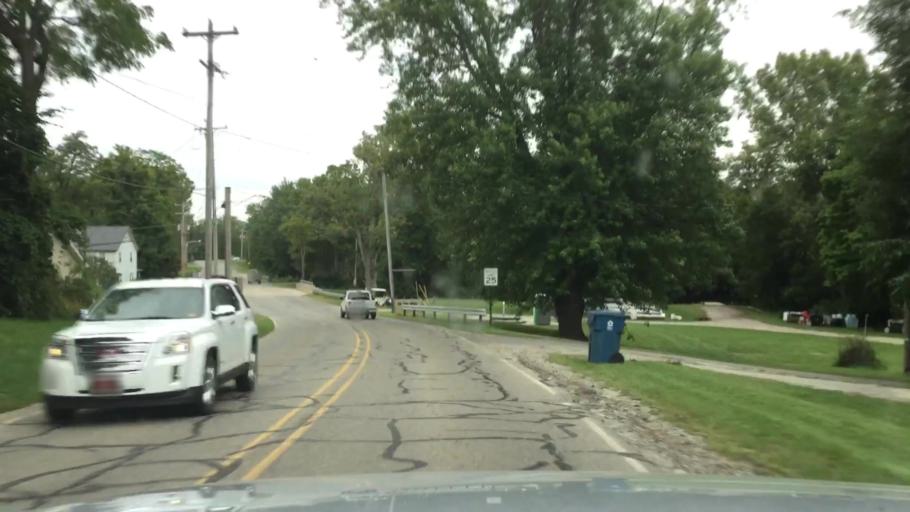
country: US
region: Michigan
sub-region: Shiawassee County
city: Durand
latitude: 42.8218
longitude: -83.9444
